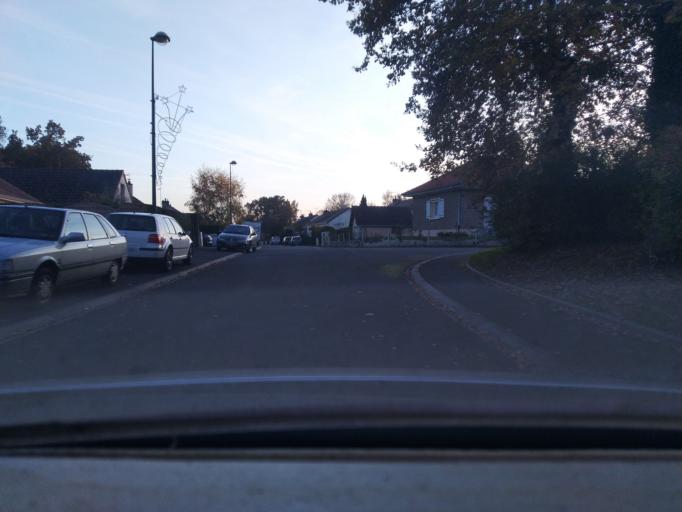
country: FR
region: Haute-Normandie
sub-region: Departement de la Seine-Maritime
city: Yainville
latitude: 49.4508
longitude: 0.8303
